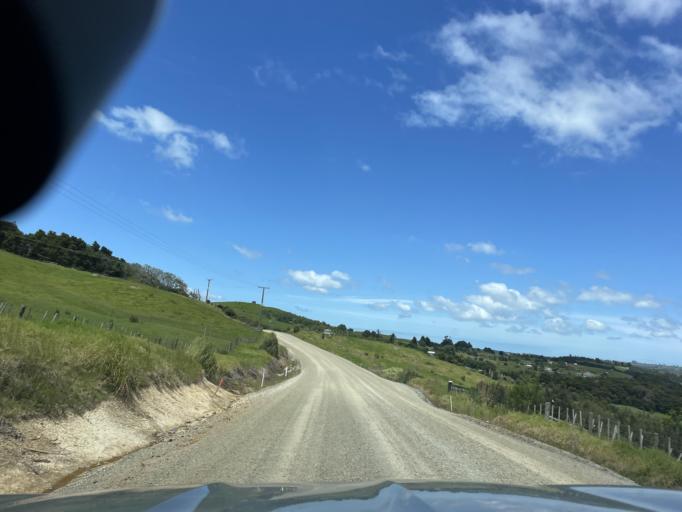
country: NZ
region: Auckland
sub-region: Auckland
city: Wellsford
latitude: -36.1635
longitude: 174.2834
